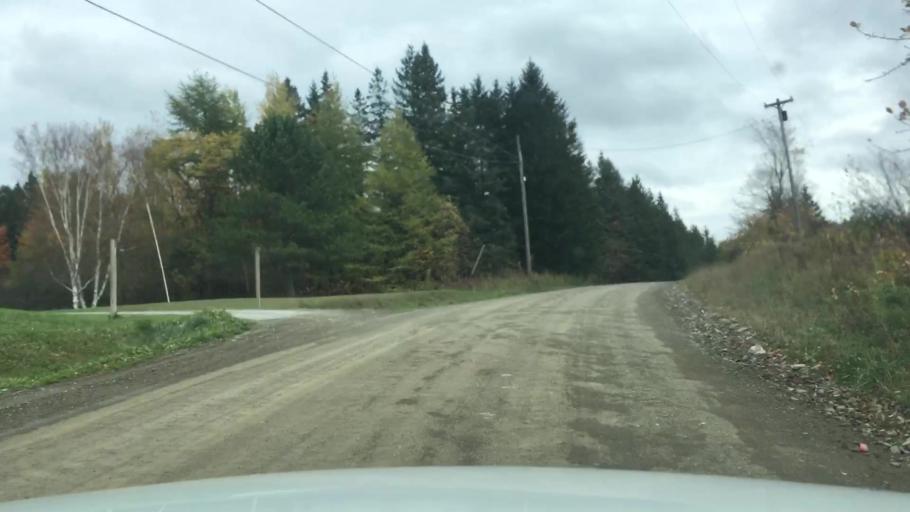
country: US
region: Maine
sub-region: Aroostook County
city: Easton
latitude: 46.5211
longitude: -67.8881
